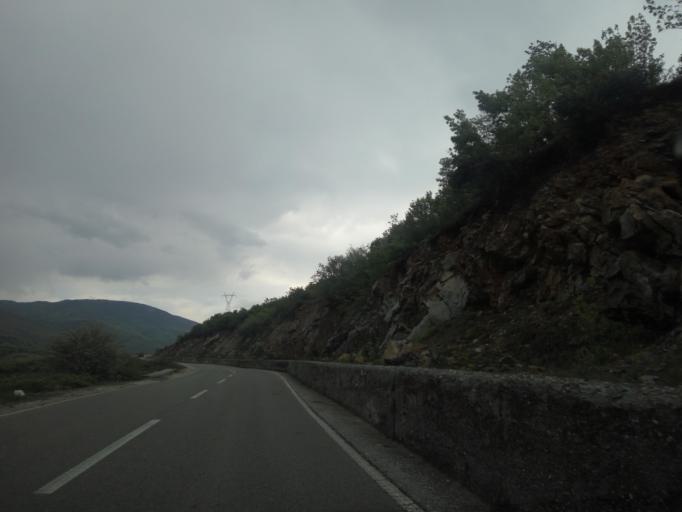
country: AL
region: Kukes
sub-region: Rrethi i Tropojes
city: Bytyc
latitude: 42.3933
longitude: 20.1833
